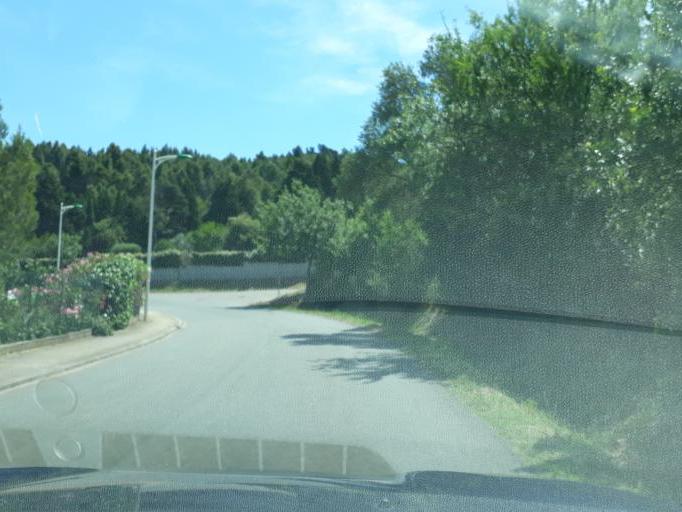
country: FR
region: Languedoc-Roussillon
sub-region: Departement de l'Aude
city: Portel-des-Corbieres
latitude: 43.0489
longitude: 2.9234
